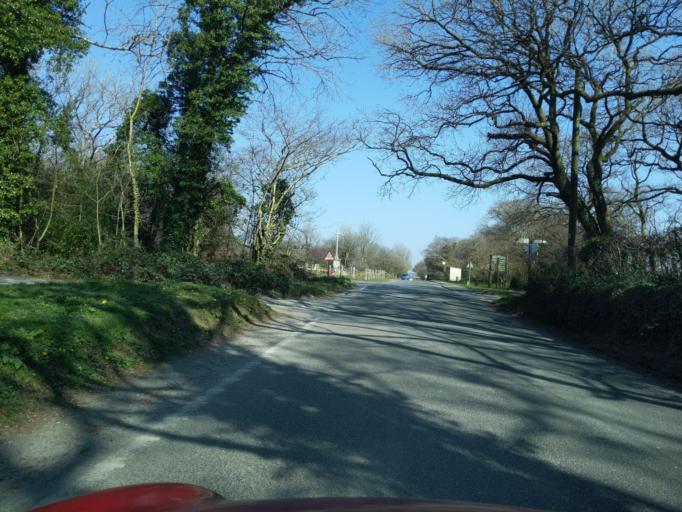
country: GB
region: England
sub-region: Devon
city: Horrabridge
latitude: 50.4908
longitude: -4.1101
